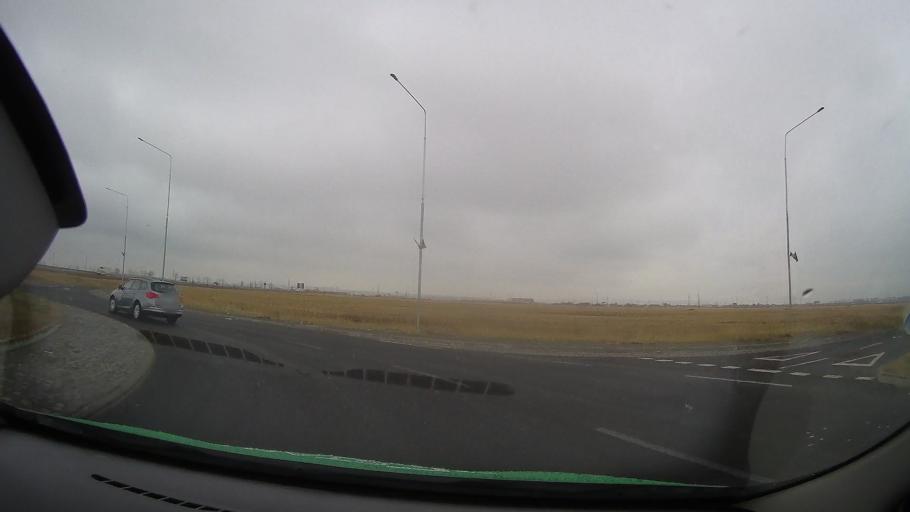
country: RO
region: Prahova
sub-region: Comuna Targsoru Vechi
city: Strejnicu
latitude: 44.9498
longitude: 25.9636
